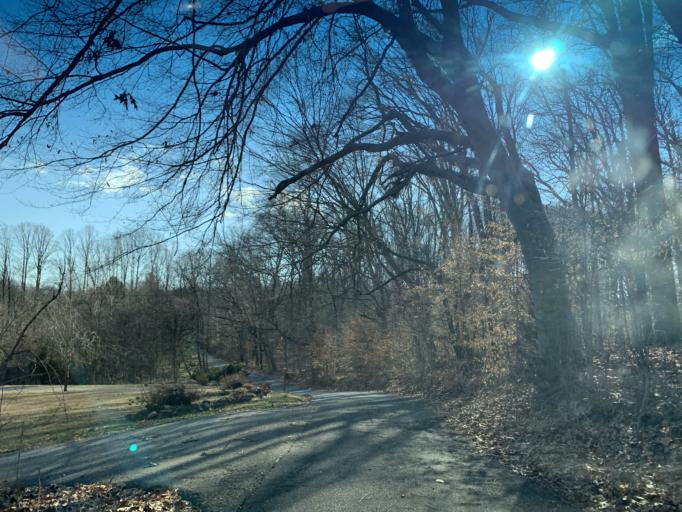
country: US
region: Maryland
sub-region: Baltimore County
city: Kingsville
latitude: 39.4302
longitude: -76.3838
